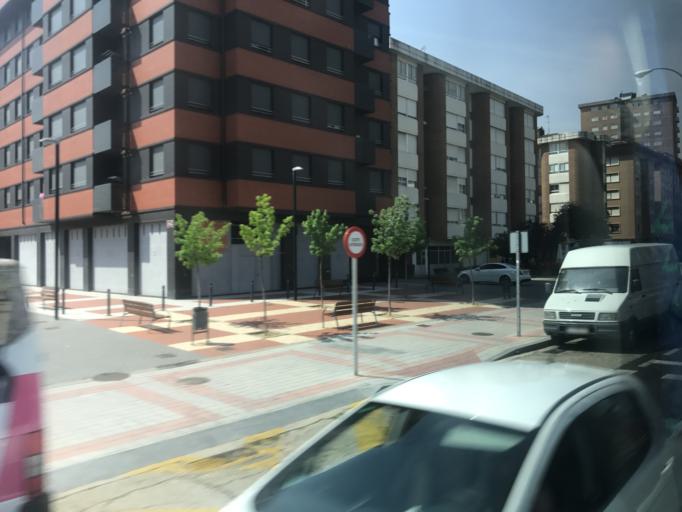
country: ES
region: Castille and Leon
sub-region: Provincia de Palencia
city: Palencia
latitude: 42.0128
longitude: -4.5225
